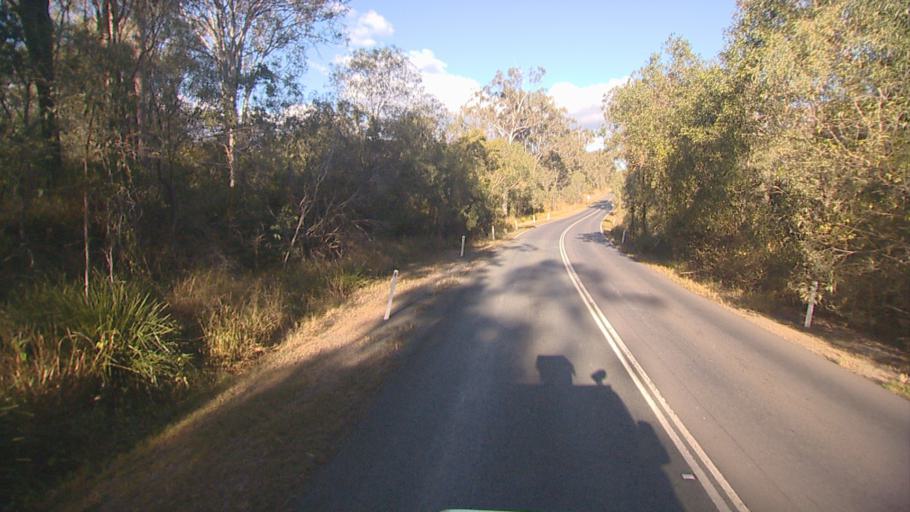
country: AU
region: Queensland
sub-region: Logan
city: Cedar Vale
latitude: -27.8864
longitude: 153.0800
